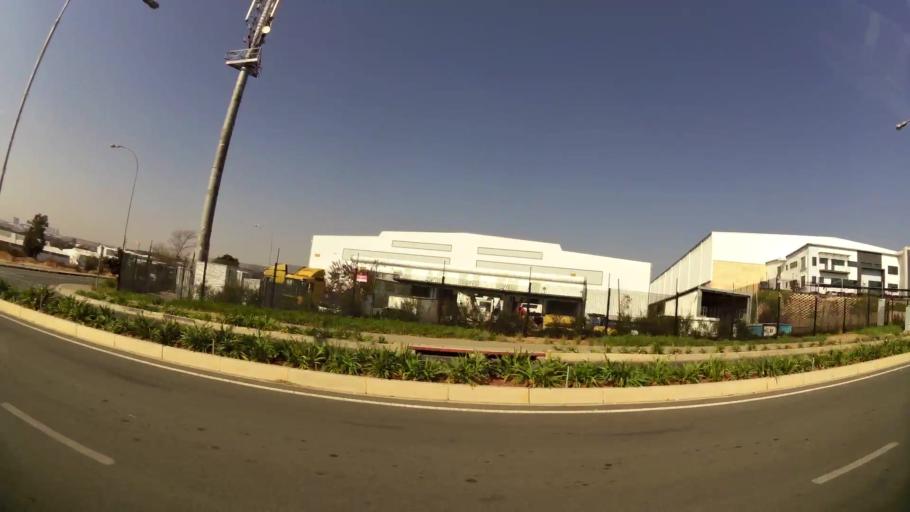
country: ZA
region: Gauteng
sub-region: City of Johannesburg Metropolitan Municipality
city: Modderfontein
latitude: -26.1002
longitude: 28.1364
